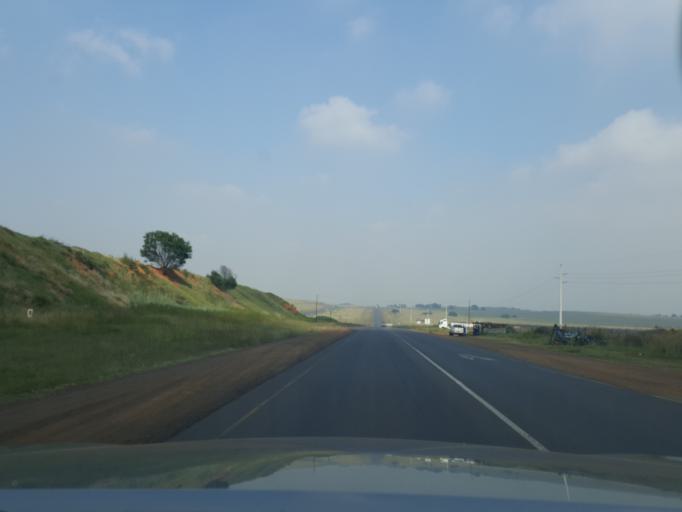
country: ZA
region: Mpumalanga
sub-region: Nkangala District Municipality
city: Witbank
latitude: -26.0145
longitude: 29.3402
